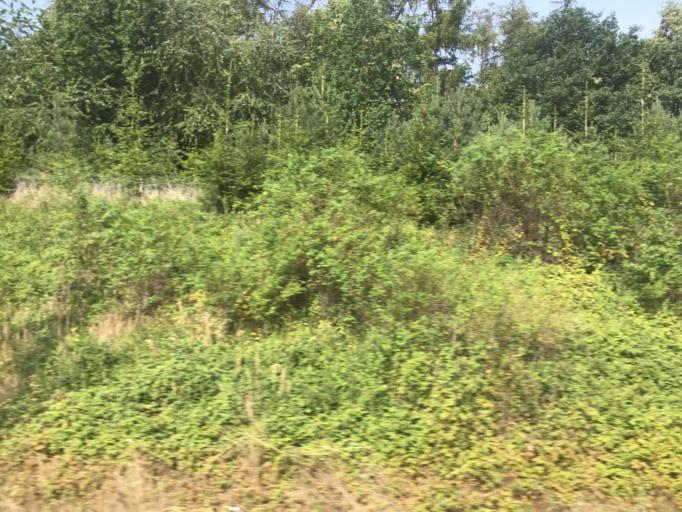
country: CZ
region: Central Bohemia
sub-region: Okres Praha-Vychod
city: Strancice
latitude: 49.9624
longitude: 14.6536
